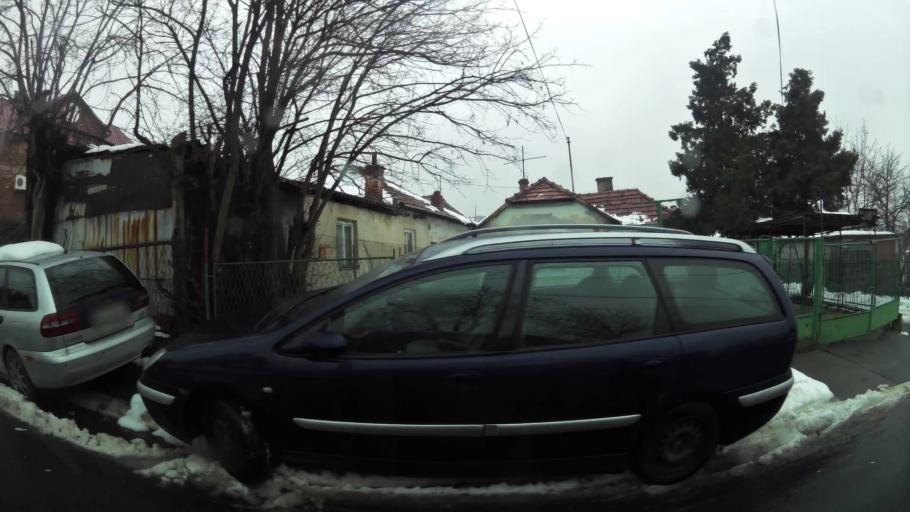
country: RS
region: Central Serbia
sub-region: Belgrade
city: Zvezdara
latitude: 44.7791
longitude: 20.5194
